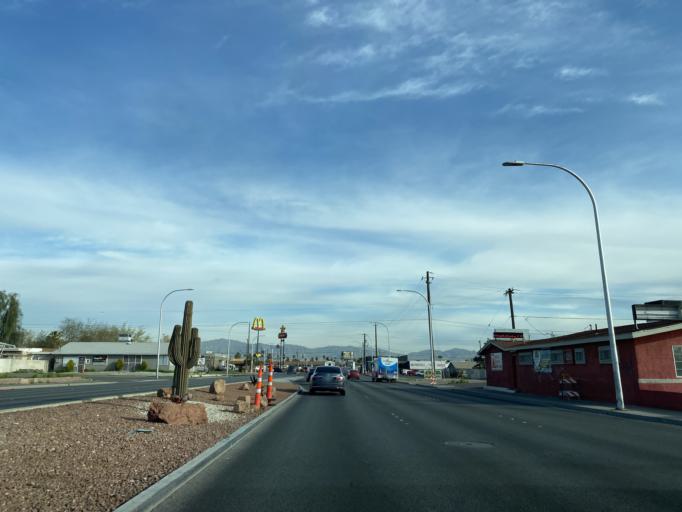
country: US
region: Nevada
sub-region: Clark County
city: Las Vegas
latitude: 36.1567
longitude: -115.1188
